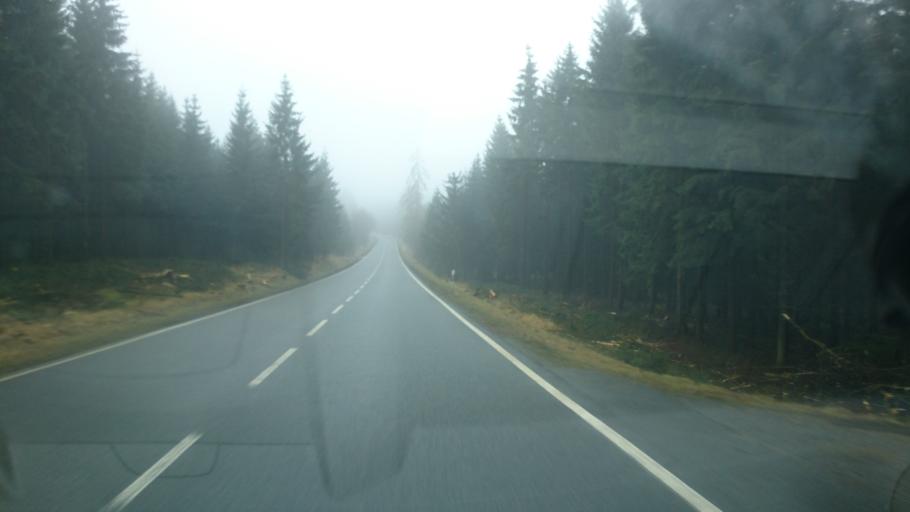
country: DE
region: Thuringia
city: Tanna
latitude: 50.4645
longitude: 11.8482
